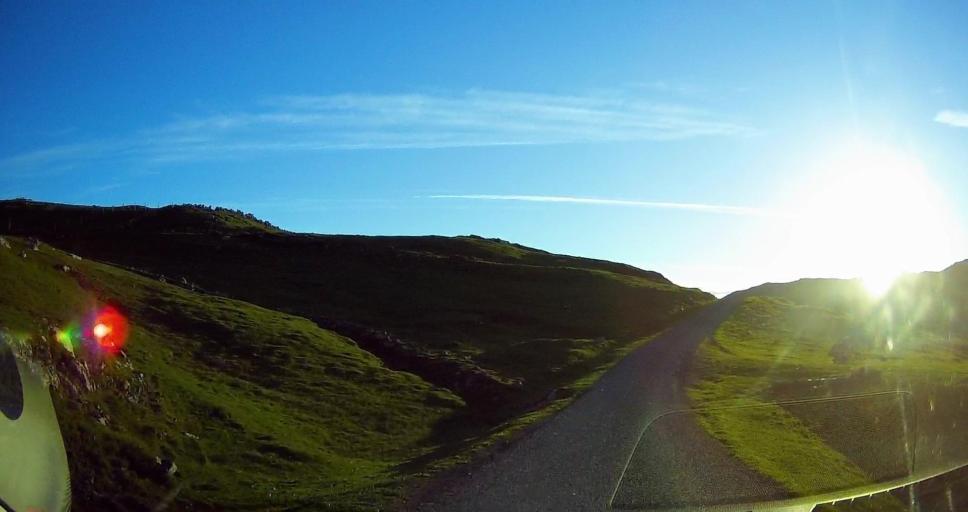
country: GB
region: Scotland
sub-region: Shetland Islands
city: Lerwick
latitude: 60.4487
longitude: -1.4189
